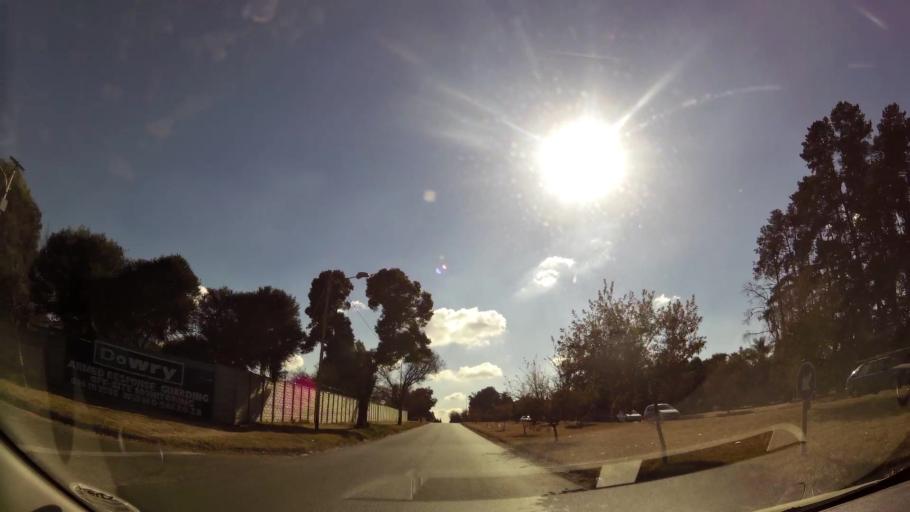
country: ZA
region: Gauteng
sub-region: City of Johannesburg Metropolitan Municipality
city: Roodepoort
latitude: -26.1405
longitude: 27.8357
